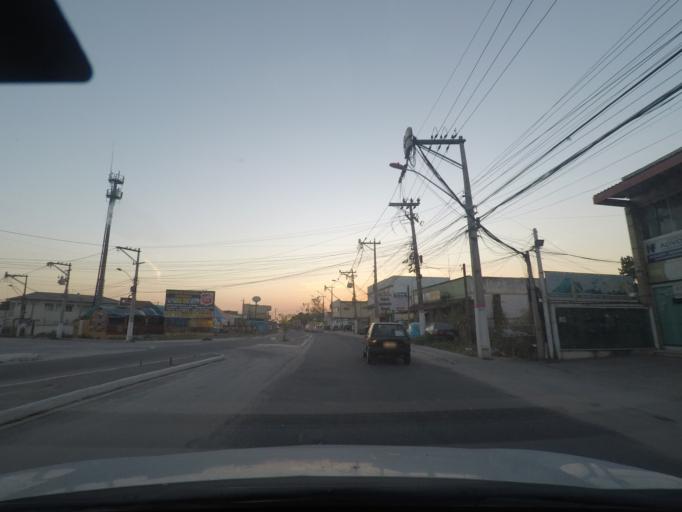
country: BR
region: Rio de Janeiro
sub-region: Niteroi
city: Niteroi
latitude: -22.9589
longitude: -42.9827
